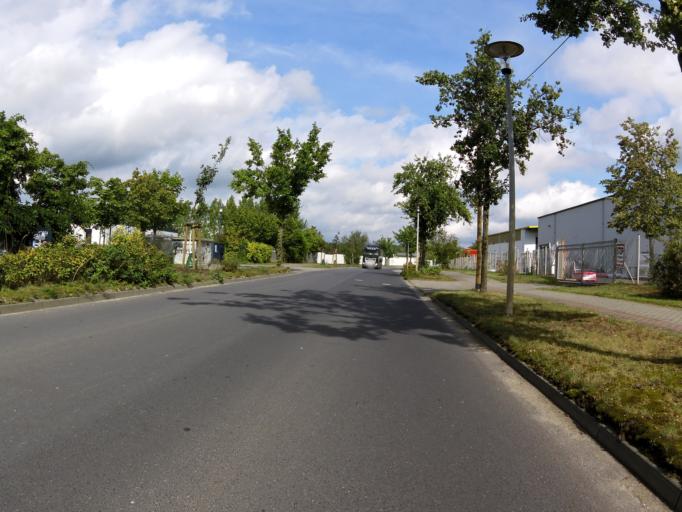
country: DE
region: Brandenburg
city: Storkow
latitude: 52.2684
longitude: 13.9377
